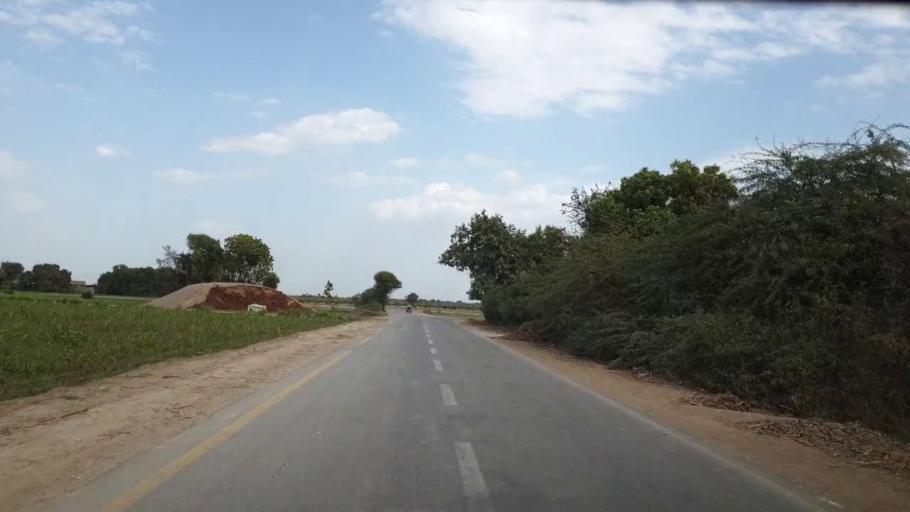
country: PK
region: Sindh
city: Tando Jam
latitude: 25.5011
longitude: 68.5967
